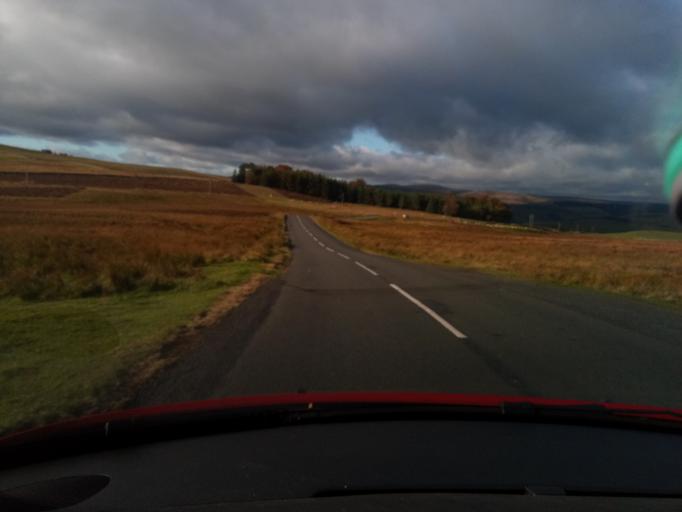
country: GB
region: Scotland
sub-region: The Scottish Borders
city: Lauder
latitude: 55.7013
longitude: -2.8208
